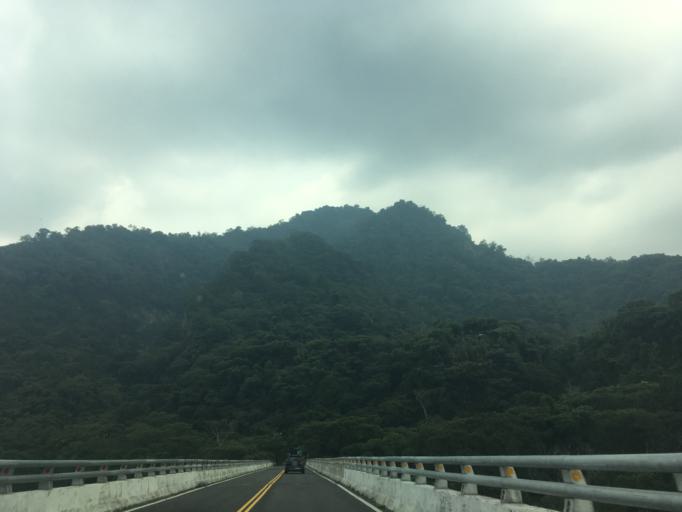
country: TW
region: Taiwan
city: Fengyuan
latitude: 24.2944
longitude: 120.9105
